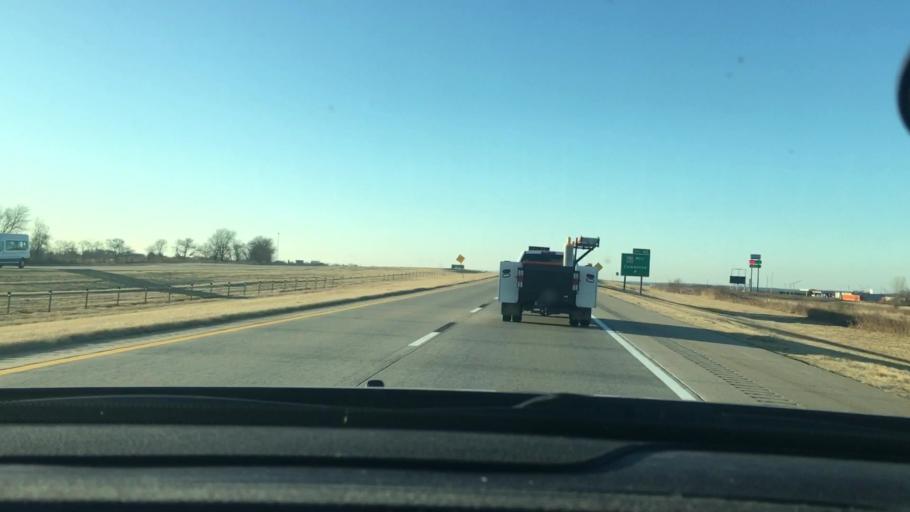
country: US
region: Oklahoma
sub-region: Carter County
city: Ardmore
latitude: 34.3379
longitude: -97.1505
